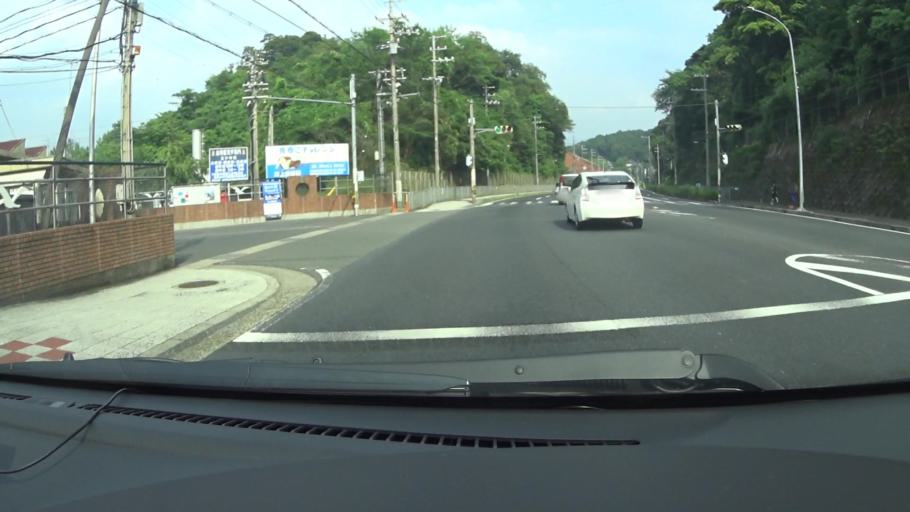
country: JP
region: Kyoto
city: Maizuru
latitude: 35.3745
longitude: 135.3205
